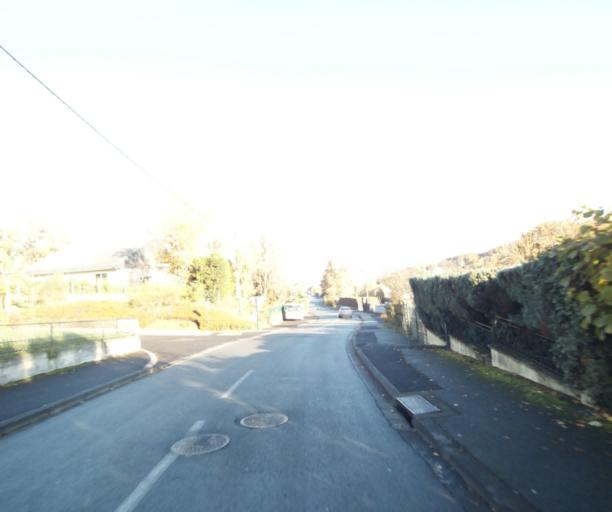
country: FR
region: Auvergne
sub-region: Departement du Puy-de-Dome
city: Durtol
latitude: 45.8020
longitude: 3.0558
